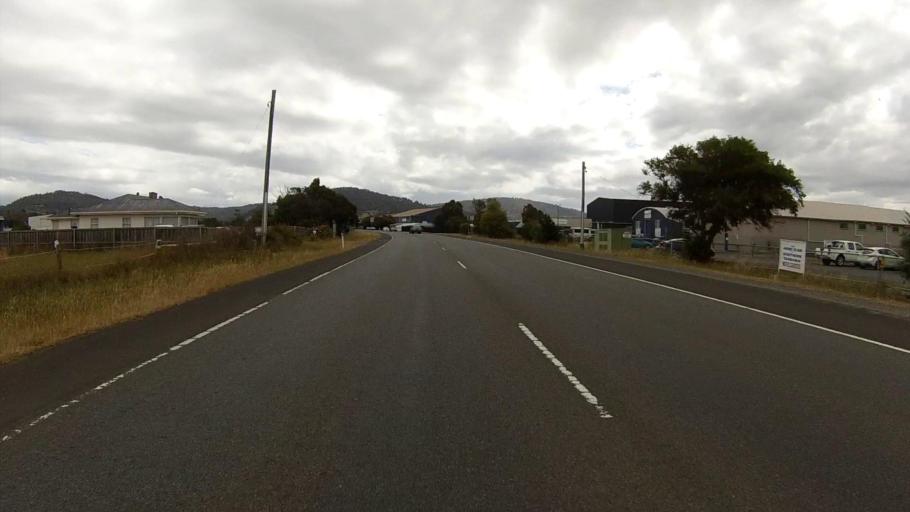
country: AU
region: Tasmania
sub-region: Clarence
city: Cambridge
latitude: -42.8302
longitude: 147.4760
